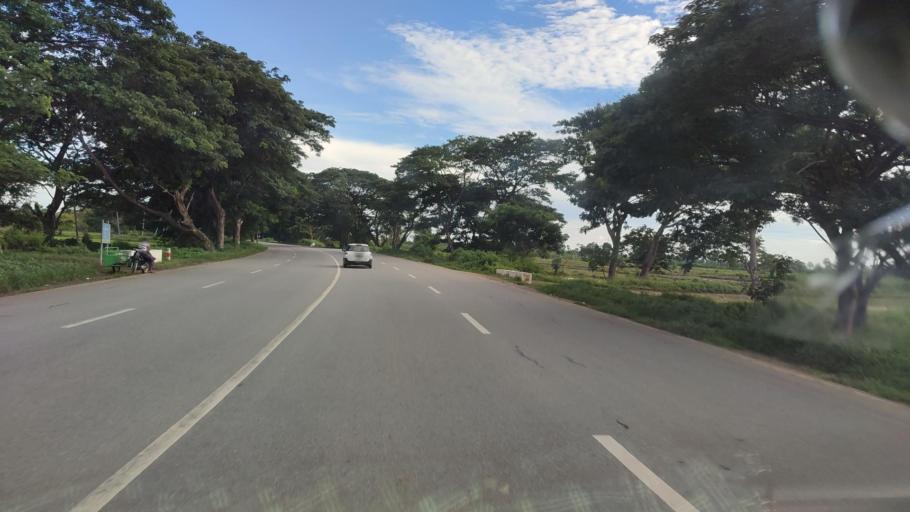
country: MM
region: Mandalay
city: Yamethin
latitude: 20.2271
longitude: 96.1792
